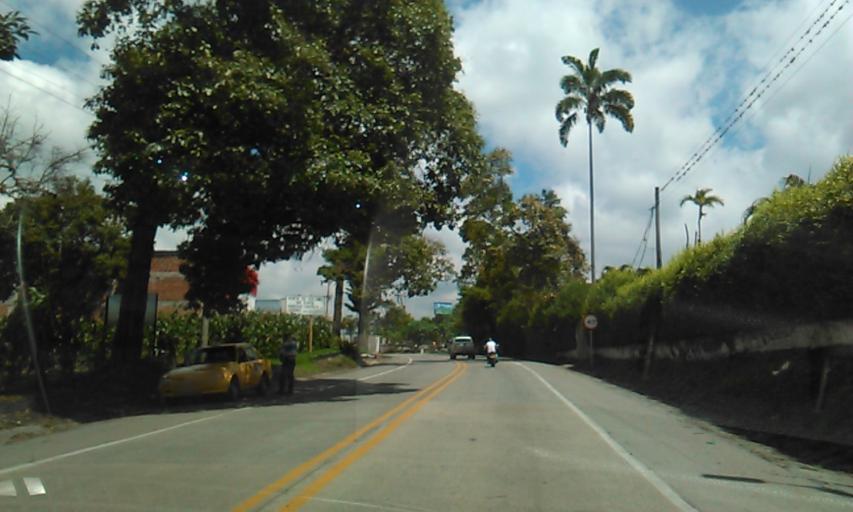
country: CO
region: Quindio
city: Armenia
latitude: 4.4982
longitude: -75.6921
